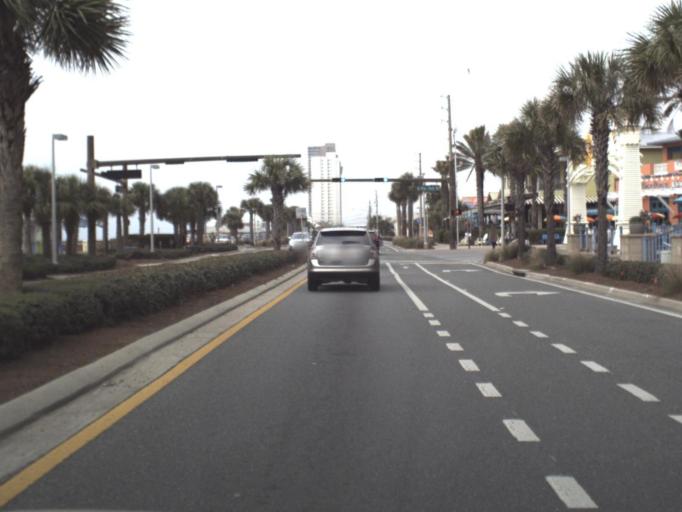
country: US
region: Florida
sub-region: Bay County
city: Laguna Beach
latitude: 30.2156
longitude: -85.8764
